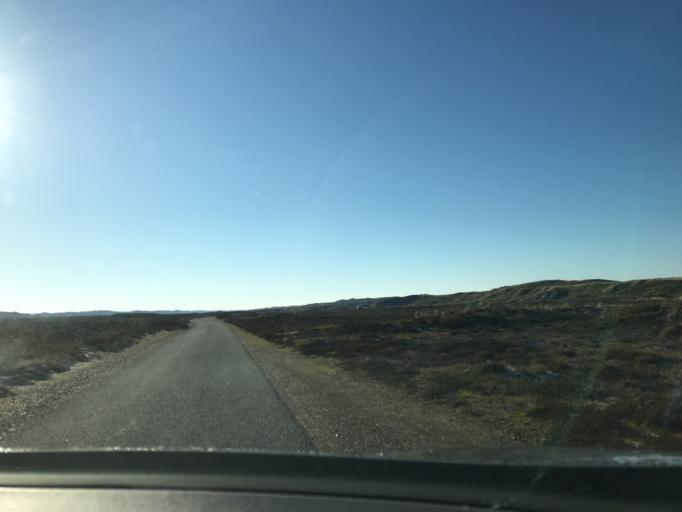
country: DK
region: South Denmark
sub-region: Varde Kommune
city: Oksbol
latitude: 55.7963
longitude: 8.1821
